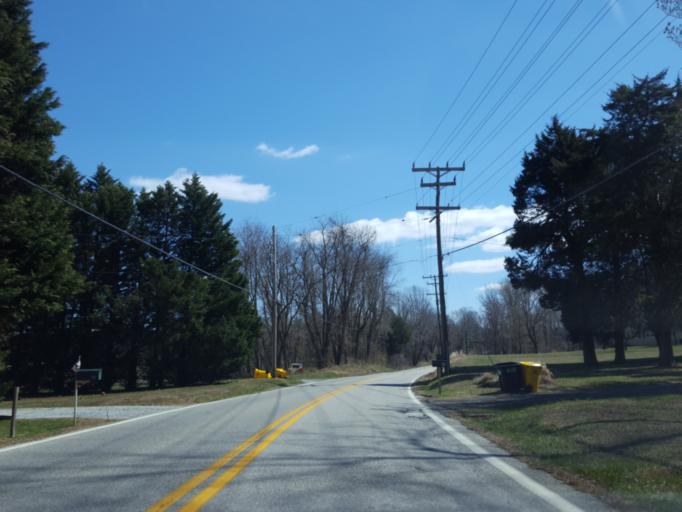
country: US
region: Maryland
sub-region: Calvert County
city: Owings
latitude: 38.7365
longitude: -76.5836
